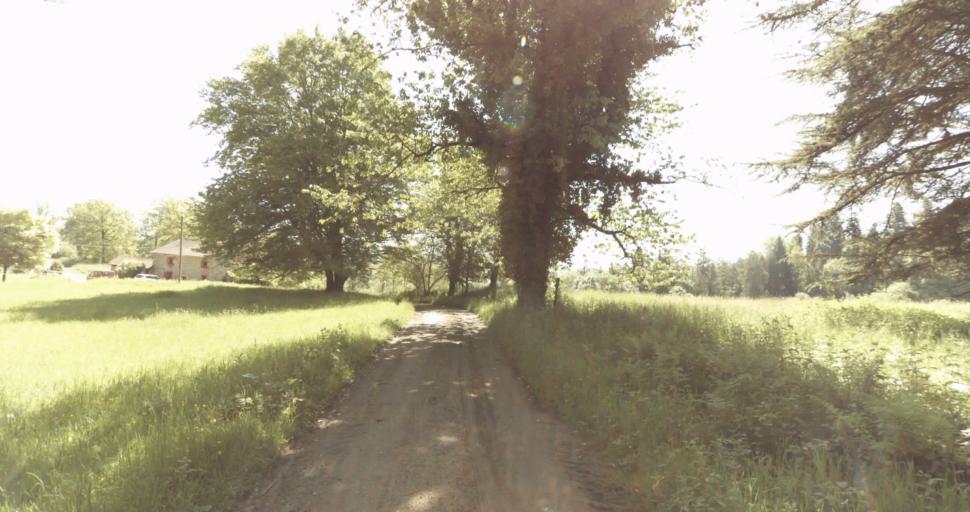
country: FR
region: Limousin
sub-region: Departement de la Haute-Vienne
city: Le Vigen
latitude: 45.7273
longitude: 1.3035
